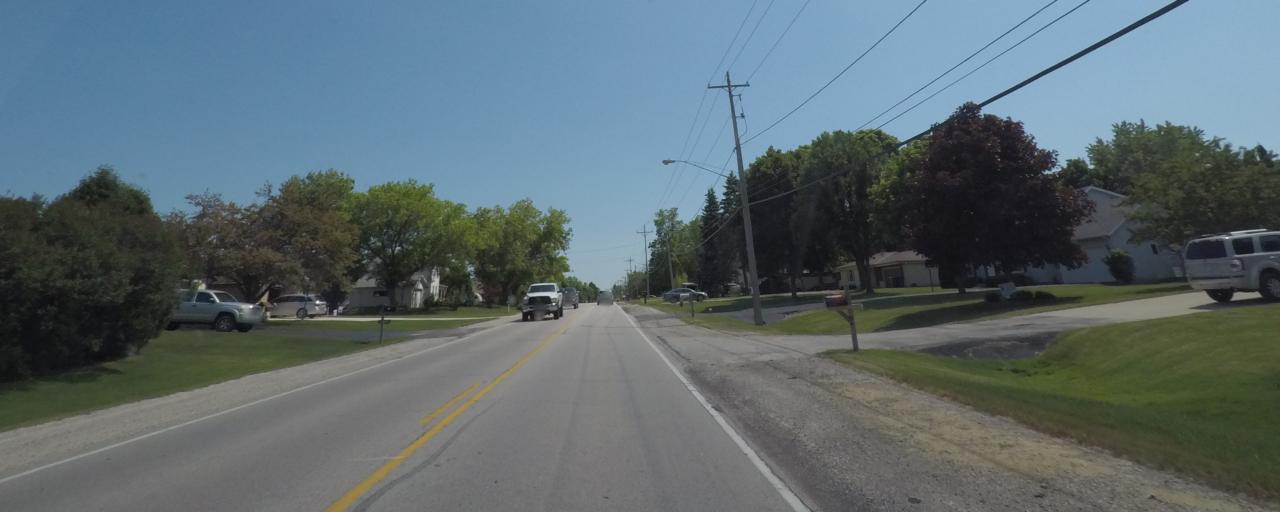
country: US
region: Wisconsin
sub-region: Milwaukee County
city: Oak Creek
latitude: 42.8969
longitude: -87.9315
